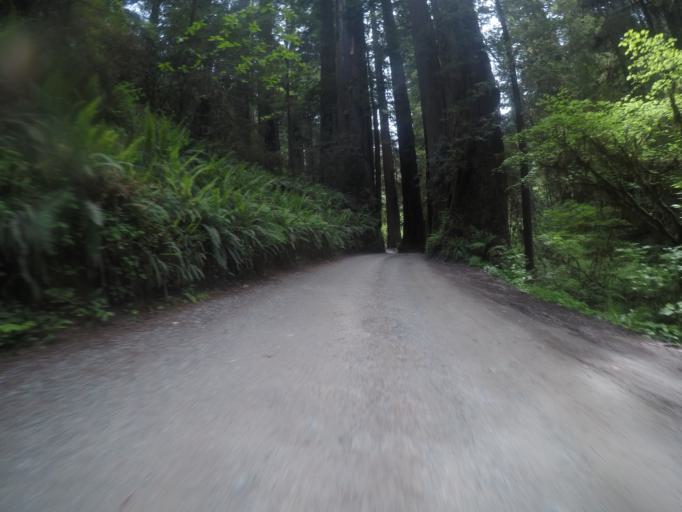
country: US
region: California
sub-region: Del Norte County
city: Bertsch-Oceanview
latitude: 41.7645
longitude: -124.1252
